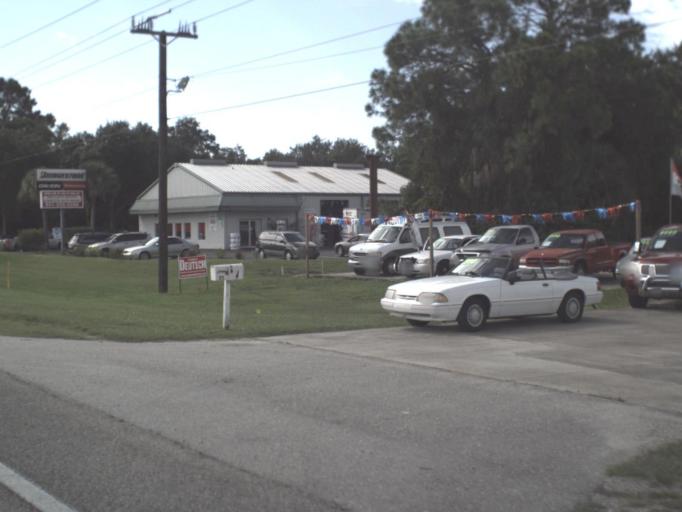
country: US
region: Florida
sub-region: Sarasota County
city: North Port
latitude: 27.0313
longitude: -82.2029
